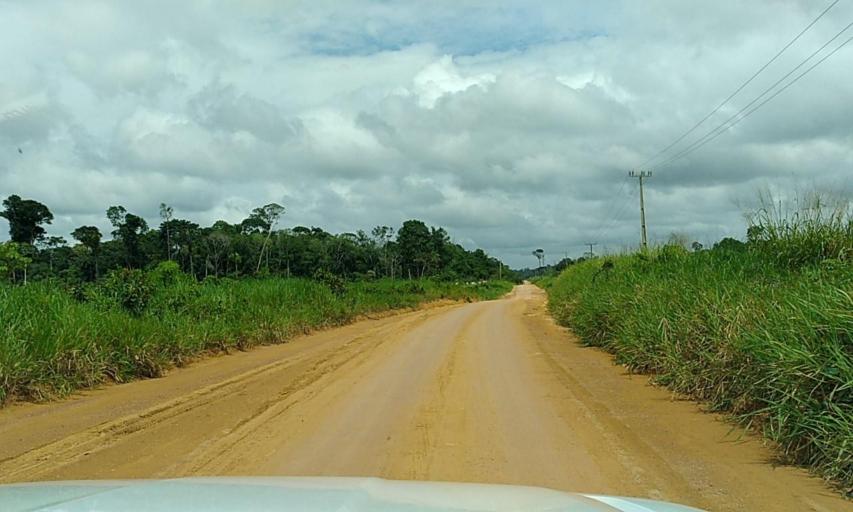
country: BR
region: Para
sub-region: Senador Jose Porfirio
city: Senador Jose Porfirio
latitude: -2.7795
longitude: -51.7747
